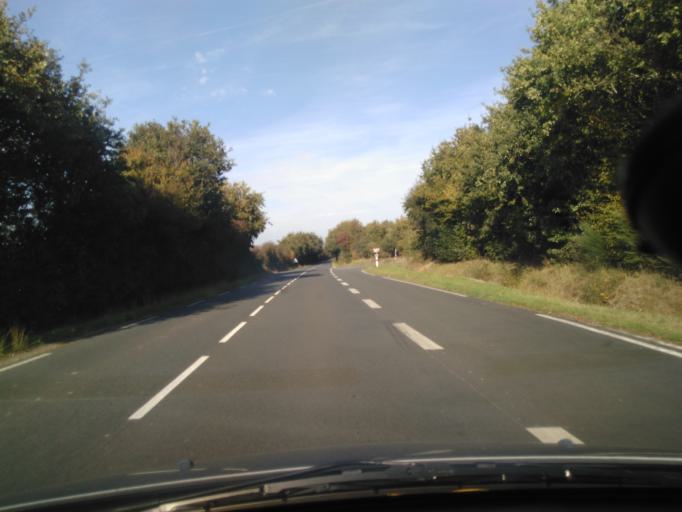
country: FR
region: Pays de la Loire
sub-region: Departement de la Vendee
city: Saint-Hilaire-de-Talmont
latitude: 46.4961
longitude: -1.5826
